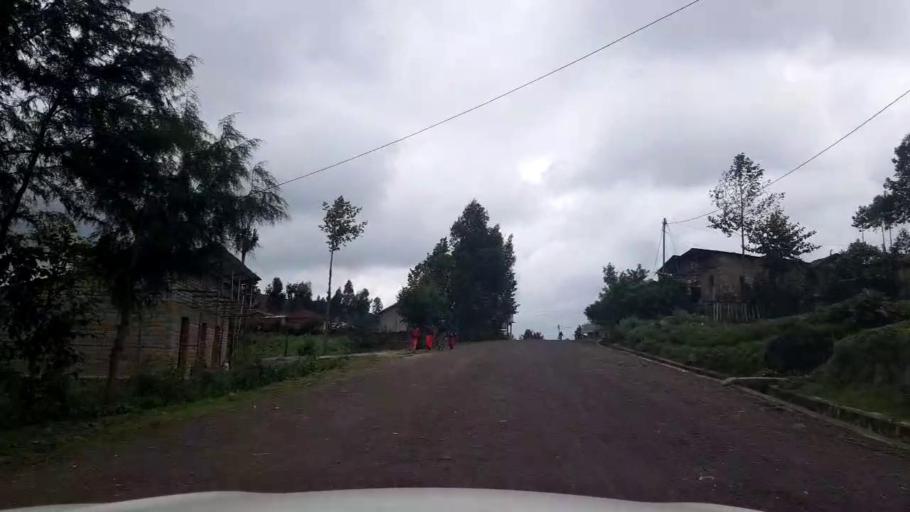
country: RW
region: Northern Province
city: Musanze
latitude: -1.5839
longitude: 29.4740
